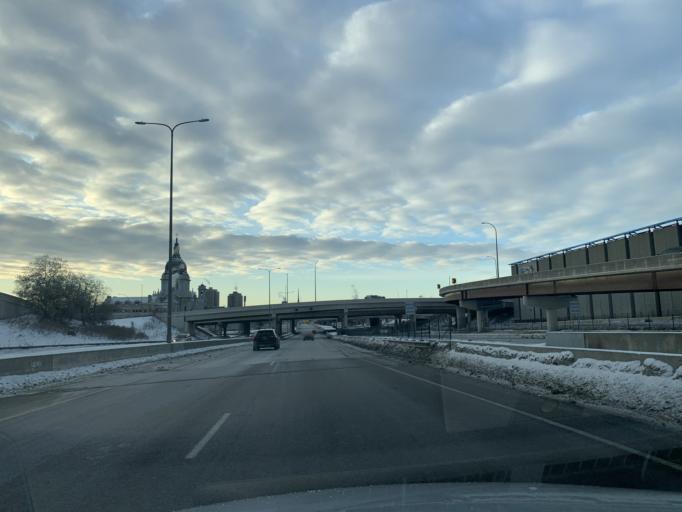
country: US
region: Minnesota
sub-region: Hennepin County
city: Minneapolis
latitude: 44.9772
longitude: -93.2875
